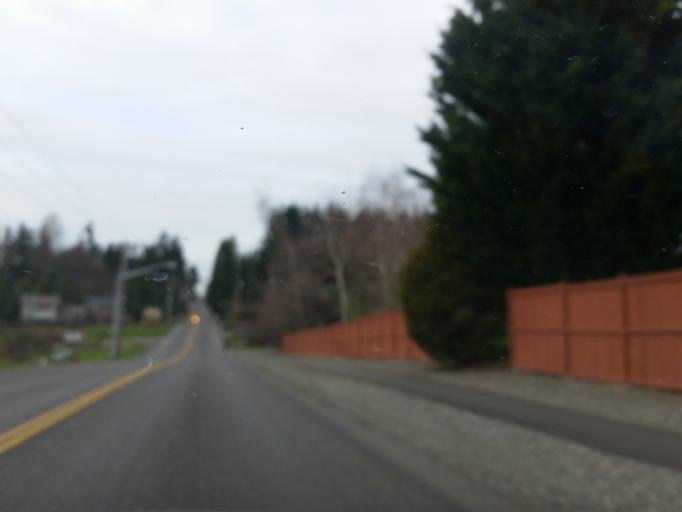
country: US
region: Washington
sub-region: Pierce County
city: South Hill
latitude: 47.1328
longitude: -122.2762
